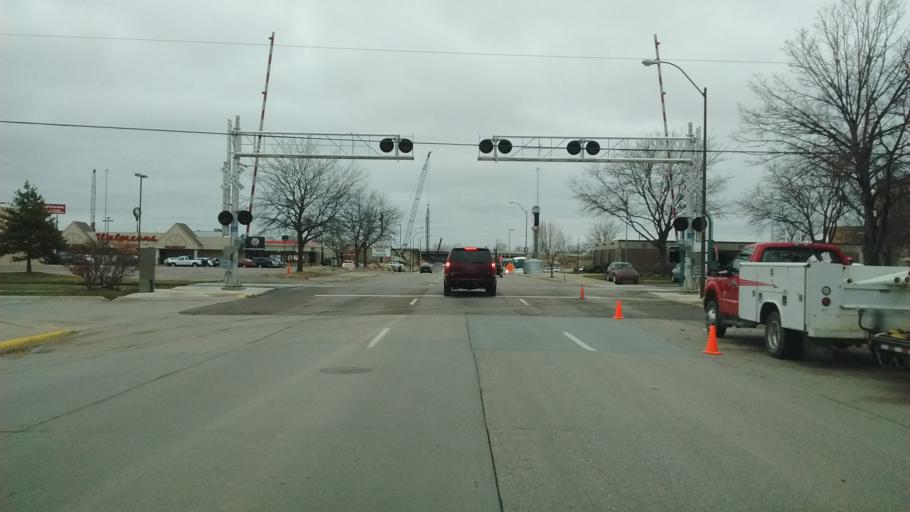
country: US
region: Iowa
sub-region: Woodbury County
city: Sioux City
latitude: 42.4922
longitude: -96.4050
